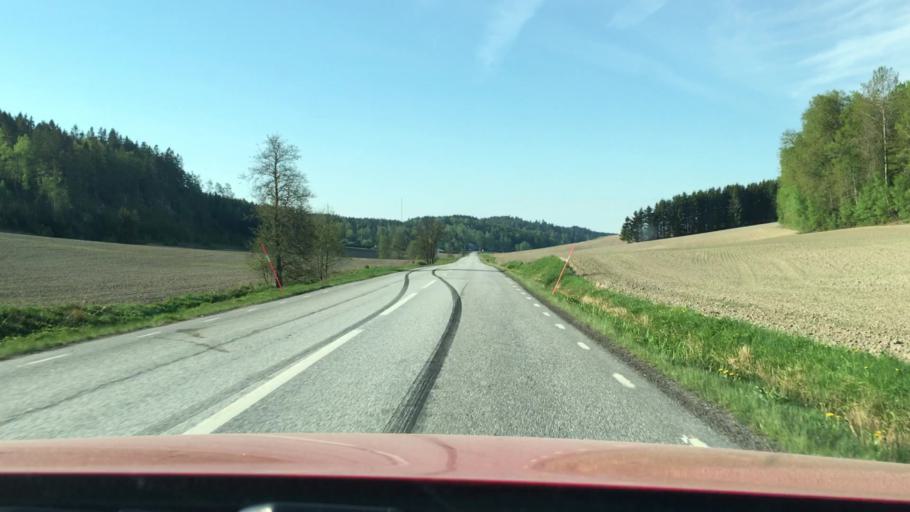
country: SE
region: Vaestra Goetaland
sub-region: Munkedals Kommun
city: Munkedal
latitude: 58.6130
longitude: 11.5587
